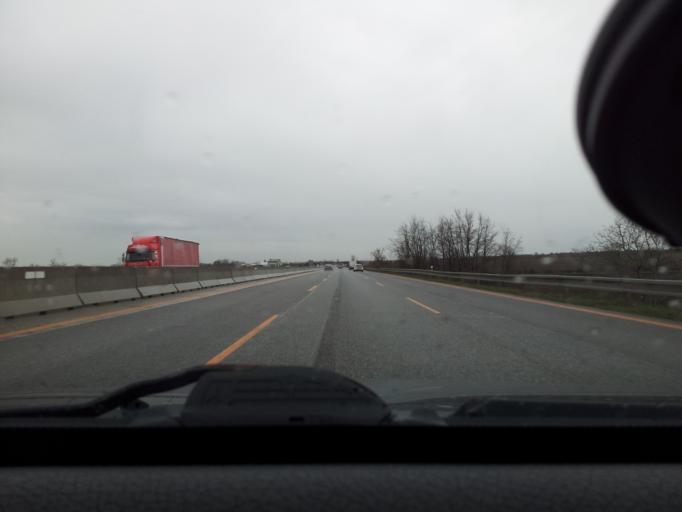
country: SK
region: Bratislavsky
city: Senec
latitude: 48.2311
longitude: 17.3569
